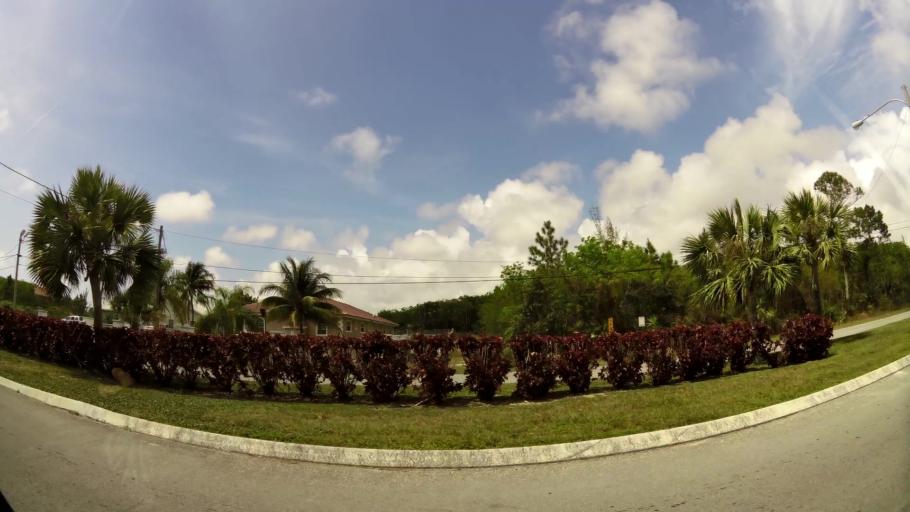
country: BS
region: Freeport
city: Freeport
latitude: 26.5033
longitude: -78.6990
